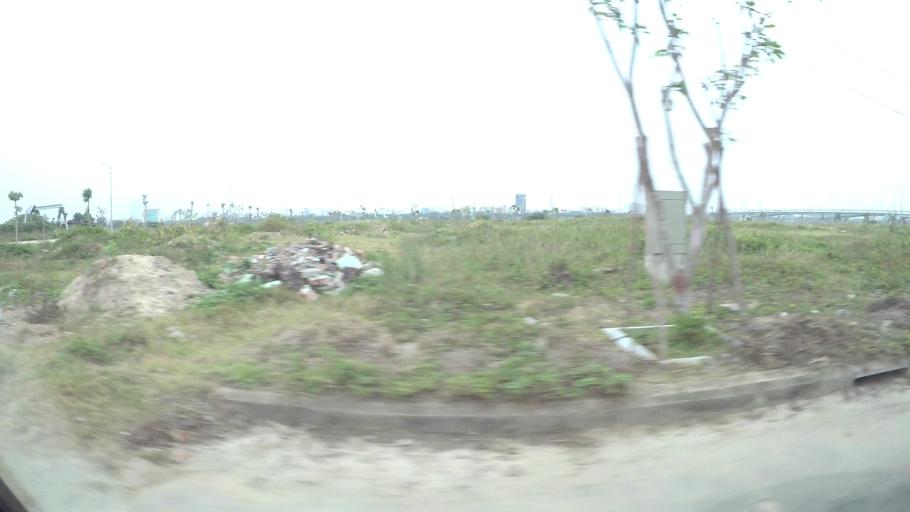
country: VN
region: Da Nang
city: Son Tra
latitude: 16.0373
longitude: 108.2329
